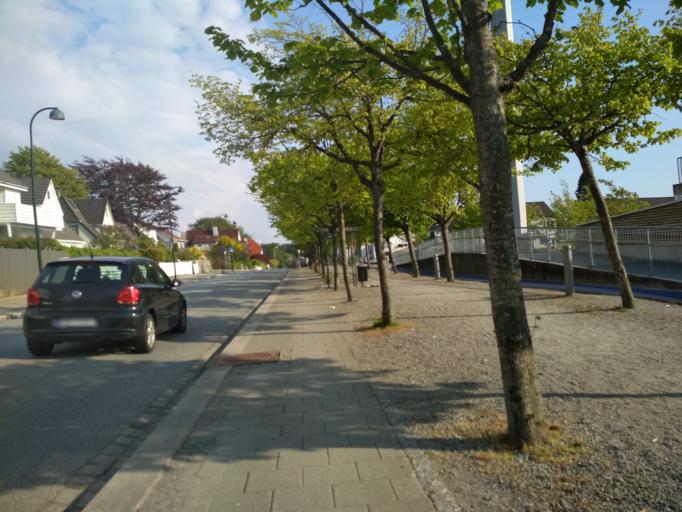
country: NO
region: Rogaland
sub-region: Stavanger
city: Stavanger
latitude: 58.9651
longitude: 5.7129
